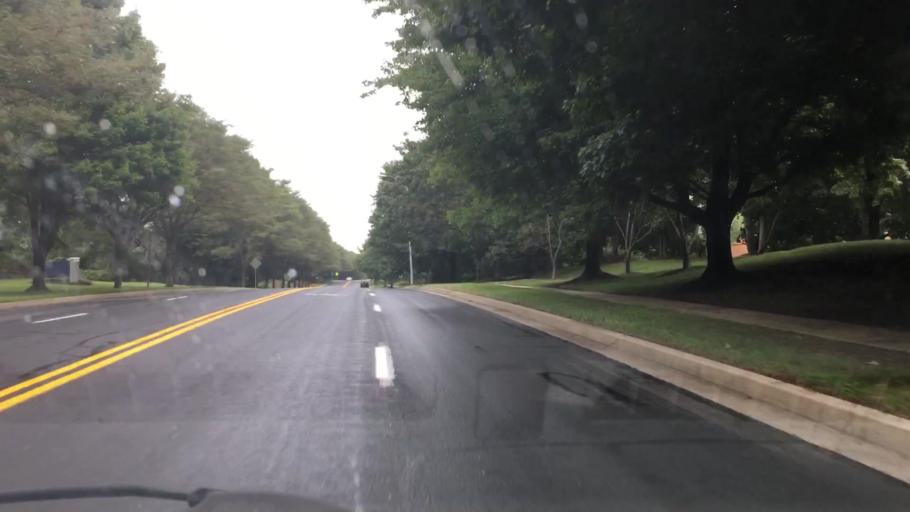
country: US
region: Maryland
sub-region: Howard County
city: Columbia
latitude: 39.1978
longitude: -76.8347
